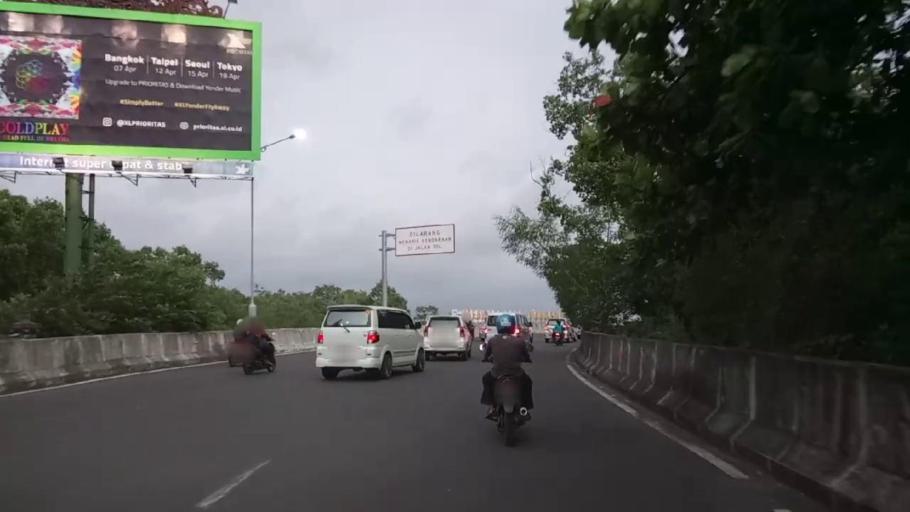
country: ID
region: Bali
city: Kelanabian
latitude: -8.7445
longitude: 115.1829
